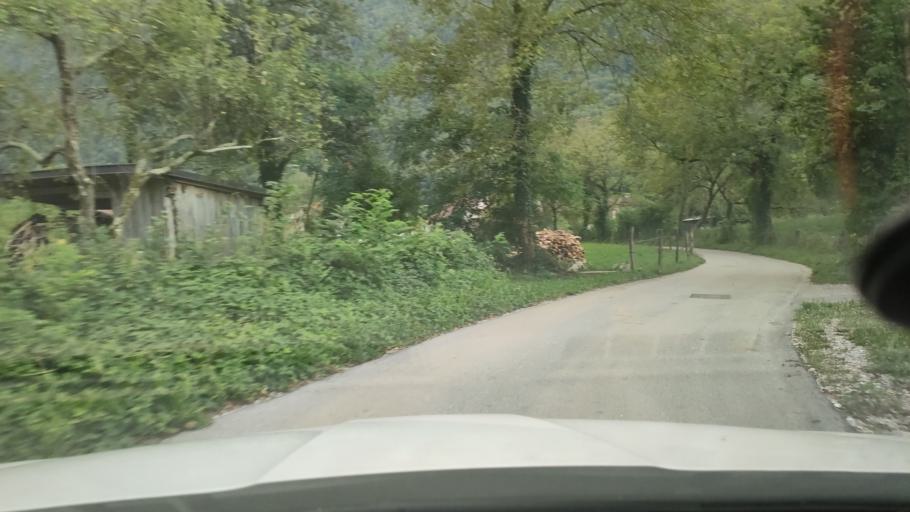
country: IT
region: Friuli Venezia Giulia
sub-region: Provincia di Udine
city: Cras
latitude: 46.2165
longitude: 13.6343
